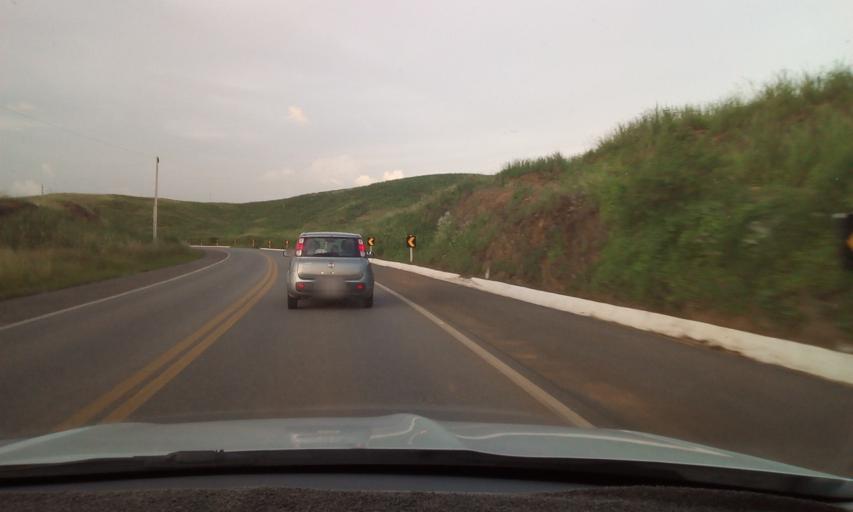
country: BR
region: Pernambuco
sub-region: Vicencia
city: Vicencia
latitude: -7.6254
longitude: -35.2422
